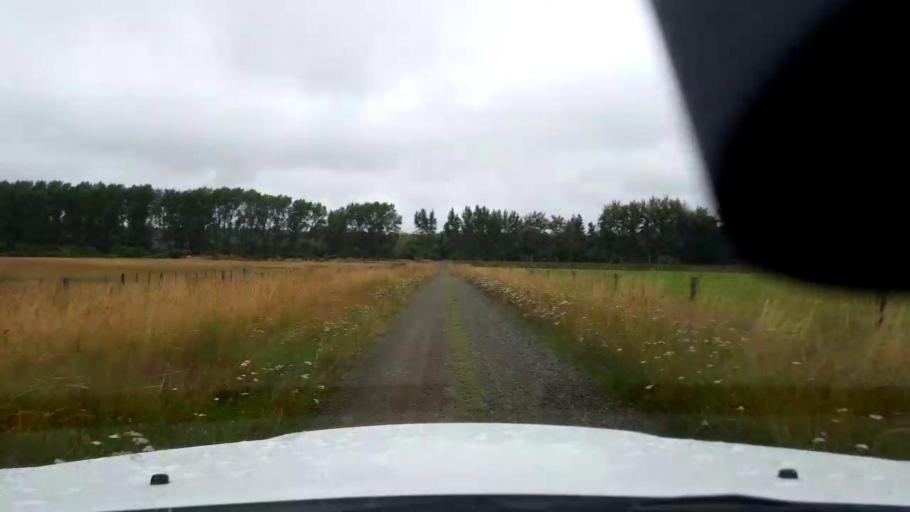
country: NZ
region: Canterbury
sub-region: Timaru District
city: Pleasant Point
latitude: -44.2582
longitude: 171.1989
